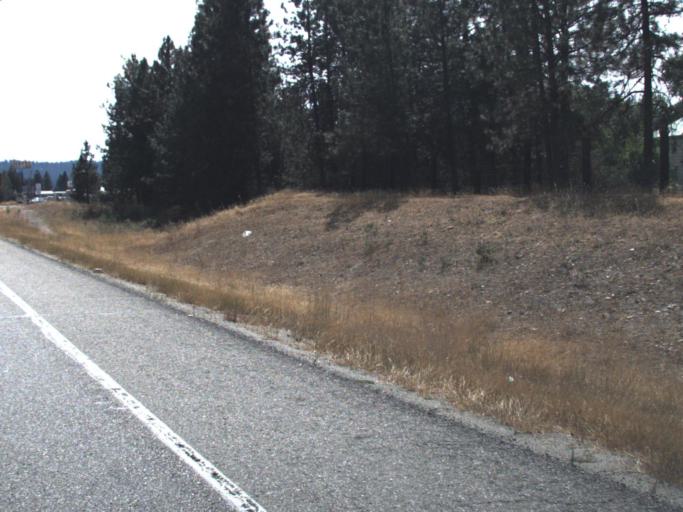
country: US
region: Washington
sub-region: Spokane County
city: Deer Park
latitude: 48.0637
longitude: -117.6224
